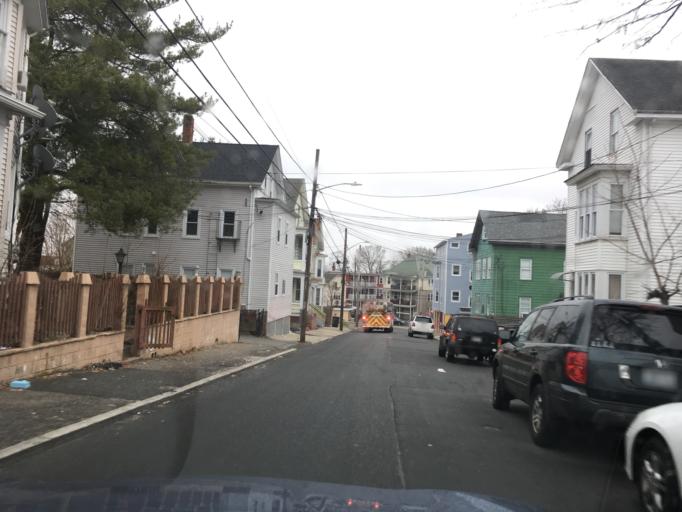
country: US
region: Rhode Island
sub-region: Providence County
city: North Providence
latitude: 41.8243
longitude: -71.4509
